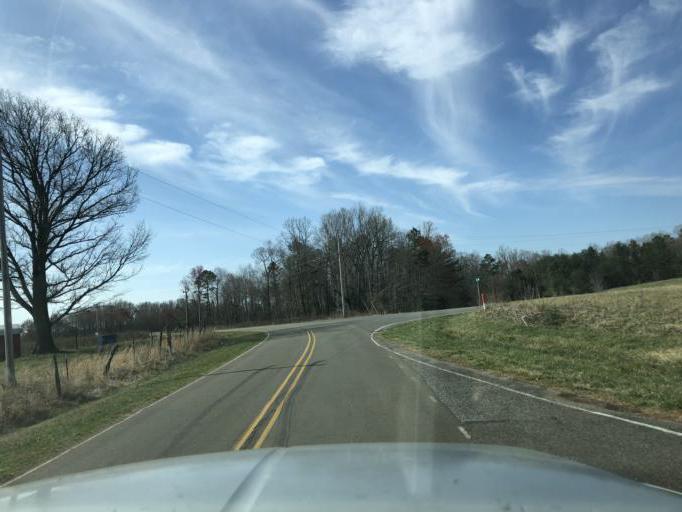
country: US
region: North Carolina
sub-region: Cleveland County
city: Shelby
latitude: 35.4801
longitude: -81.6419
